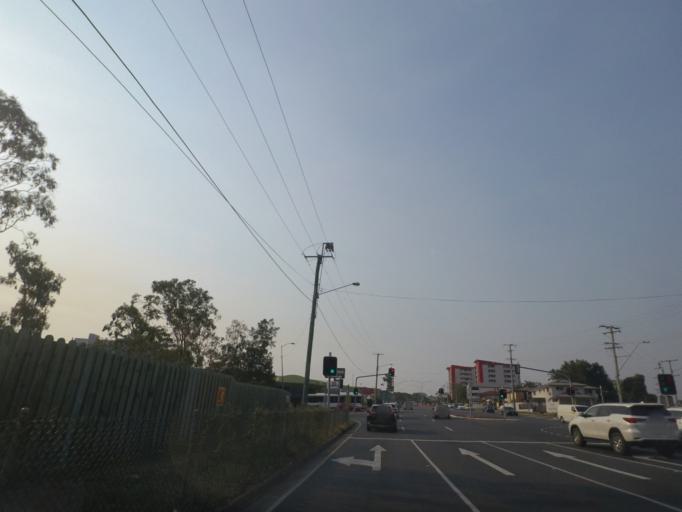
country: AU
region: Queensland
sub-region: Brisbane
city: Upper Mount Gravatt
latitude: -27.5668
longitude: 153.0880
